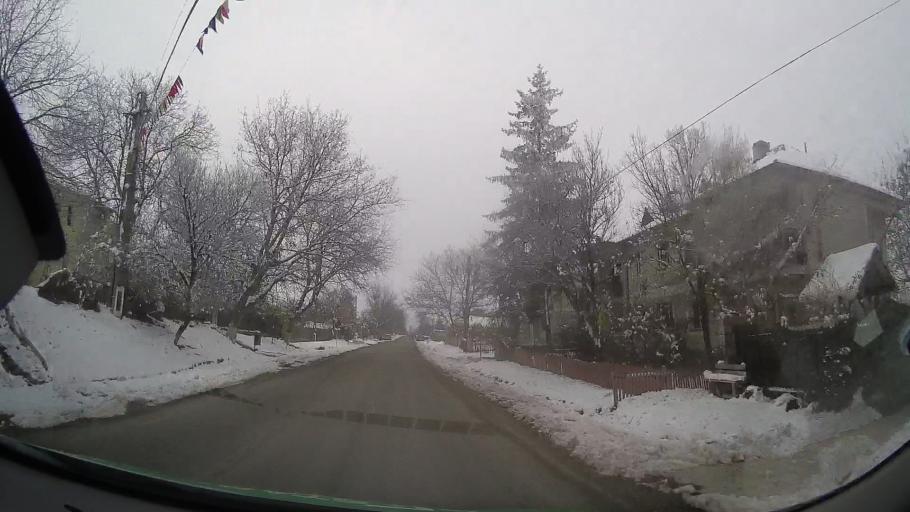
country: RO
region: Bacau
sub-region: Comuna Stanisesti
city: Stanisesti
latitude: 46.4066
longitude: 27.2723
